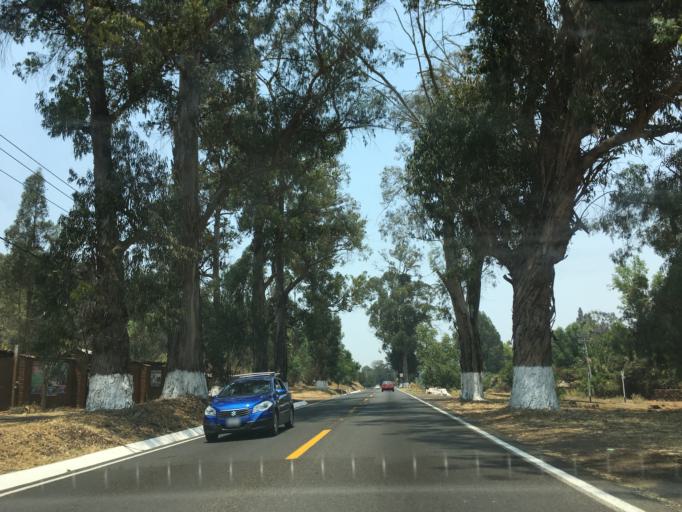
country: MX
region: Michoacan
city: Patzcuaro
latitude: 19.5449
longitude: -101.6029
